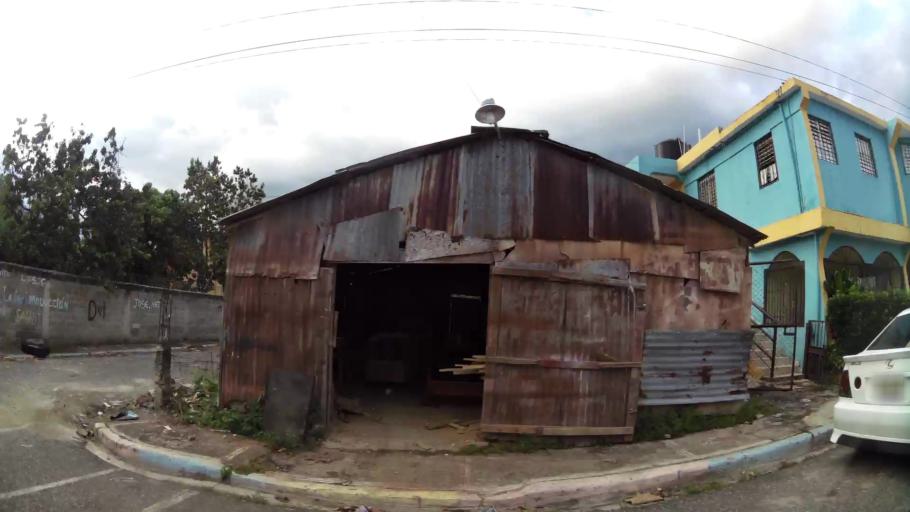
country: DO
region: San Cristobal
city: Villa Altagracia
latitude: 18.6697
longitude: -70.1665
